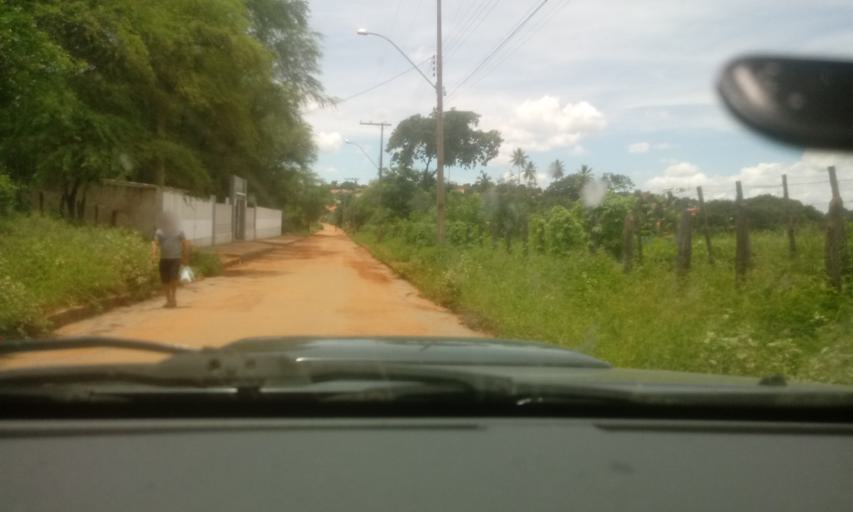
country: BR
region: Bahia
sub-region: Riacho De Santana
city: Riacho de Santana
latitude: -13.6059
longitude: -42.9456
